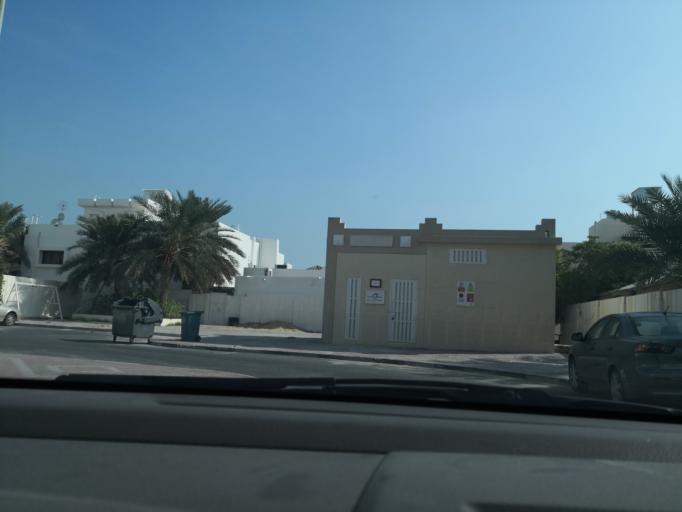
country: QA
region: Baladiyat ad Dawhah
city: Doha
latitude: 25.3303
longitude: 51.5095
